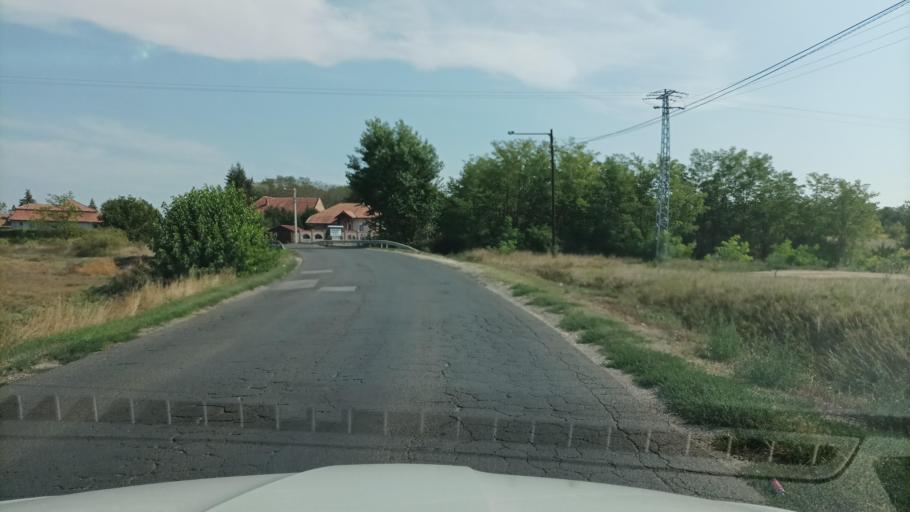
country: HU
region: Pest
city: Hevizgyoerk
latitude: 47.6225
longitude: 19.5356
